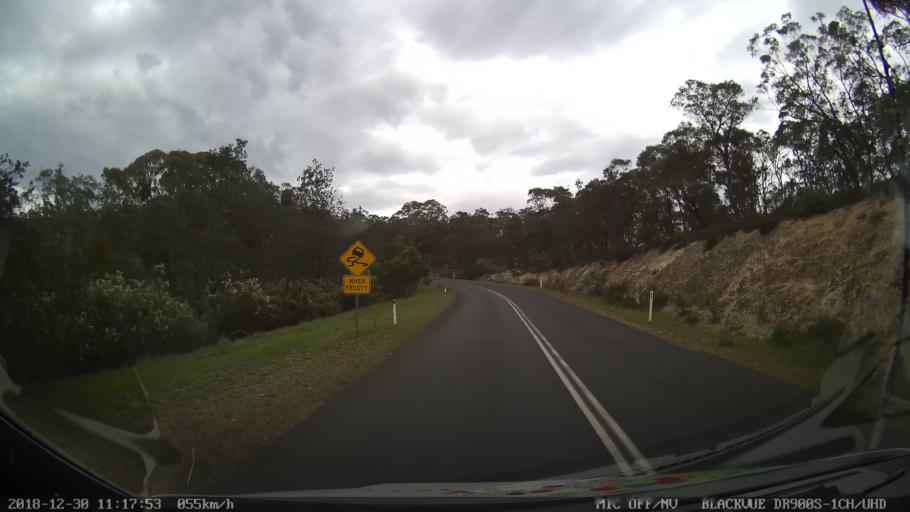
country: AU
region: New South Wales
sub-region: Snowy River
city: Jindabyne
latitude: -36.5356
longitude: 148.6956
